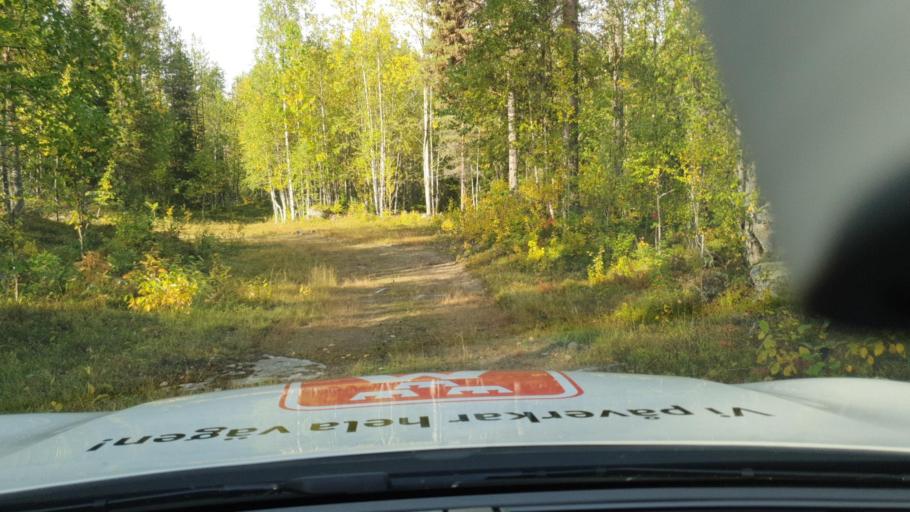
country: SE
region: Vaesterbotten
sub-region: Asele Kommun
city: Asele
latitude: 63.9279
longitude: 17.7171
